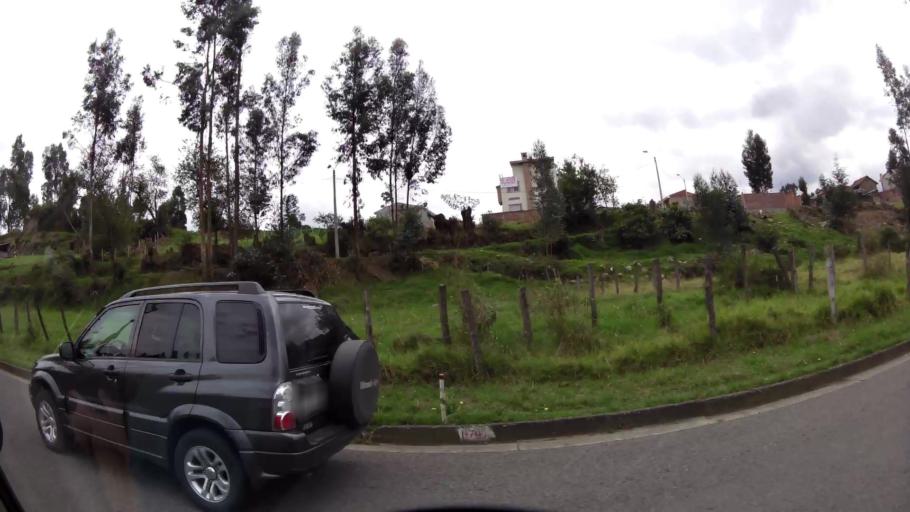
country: EC
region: Azuay
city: Cuenca
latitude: -2.9001
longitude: -79.0467
